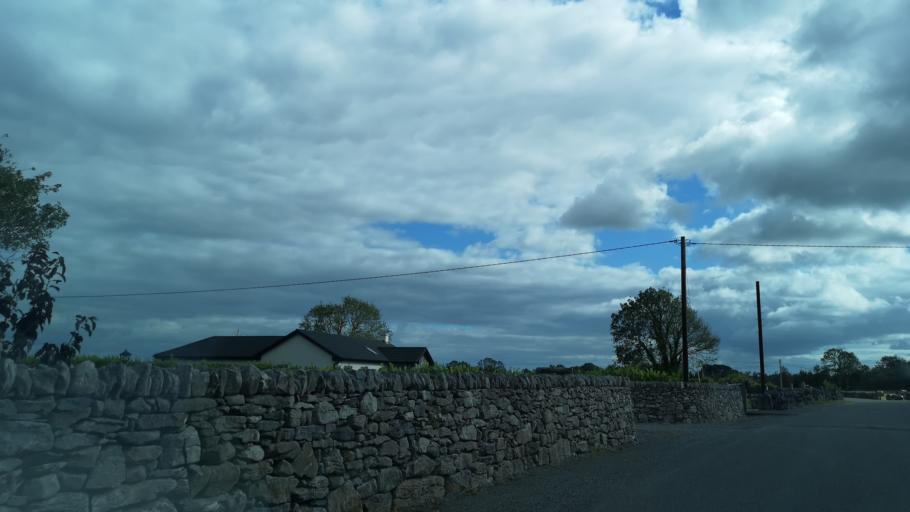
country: IE
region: Connaught
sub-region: County Galway
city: Moycullen
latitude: 53.3579
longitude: -9.1746
